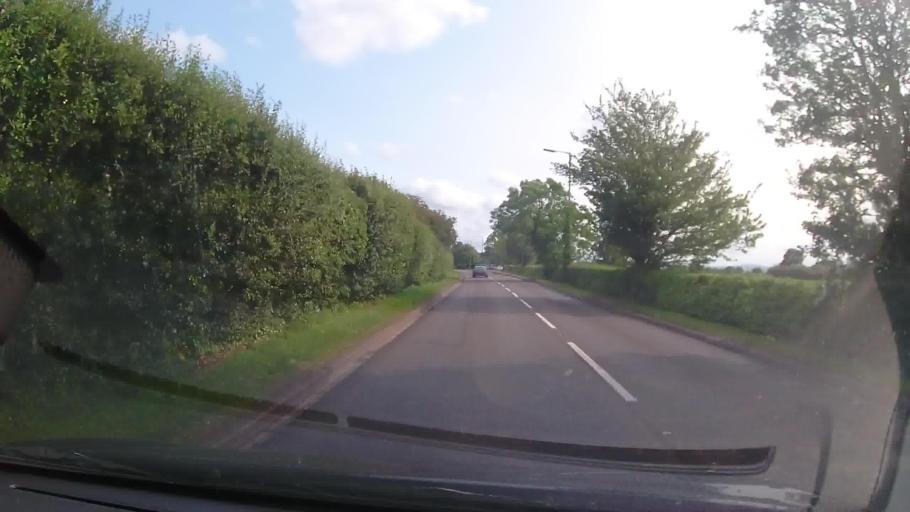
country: GB
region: England
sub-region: Shropshire
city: Shrewsbury
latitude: 52.7409
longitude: -2.7453
